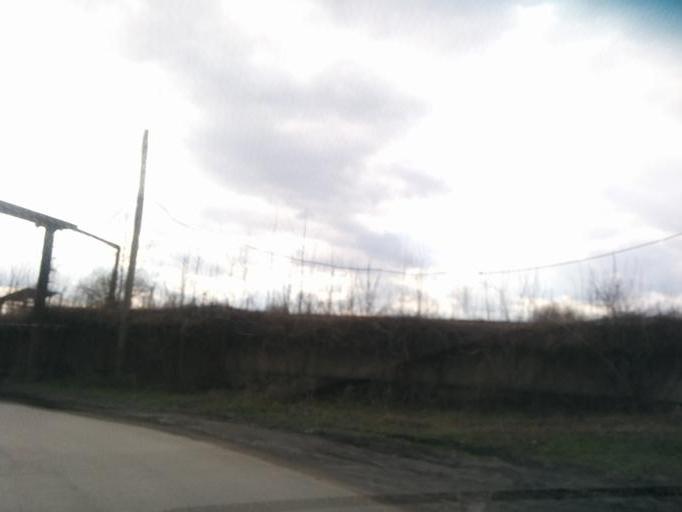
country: RU
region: Rostov
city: Shakhty
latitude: 47.6828
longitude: 40.2842
